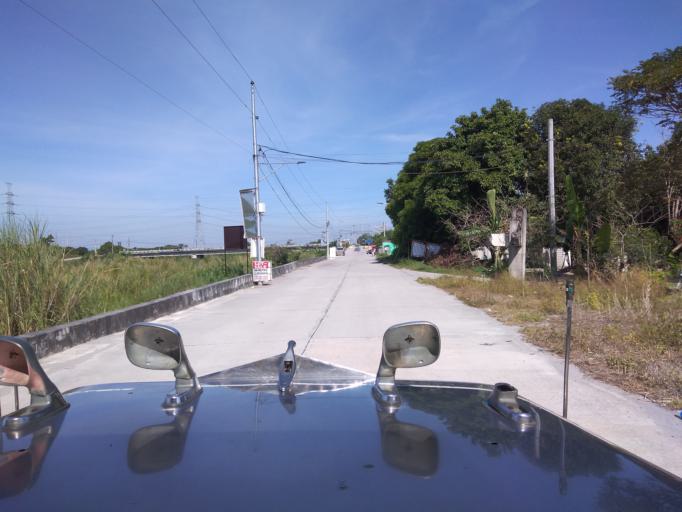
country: PH
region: Central Luzon
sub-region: Province of Pampanga
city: Bacolor
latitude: 15.0056
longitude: 120.6595
